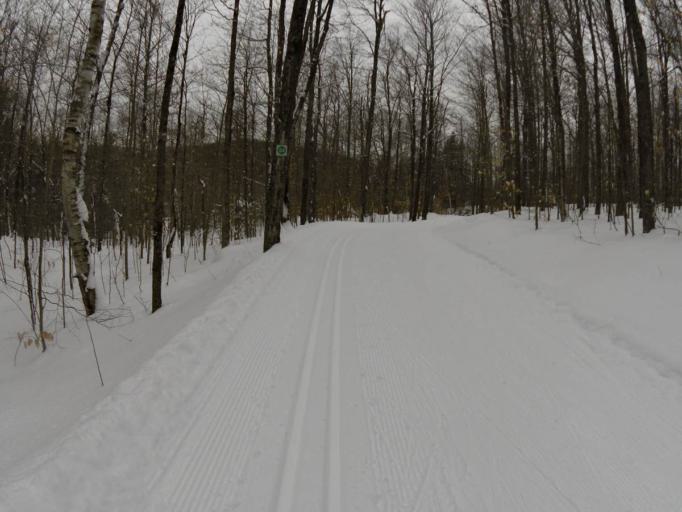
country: CA
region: Quebec
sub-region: Outaouais
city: Wakefield
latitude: 45.5922
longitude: -76.0104
